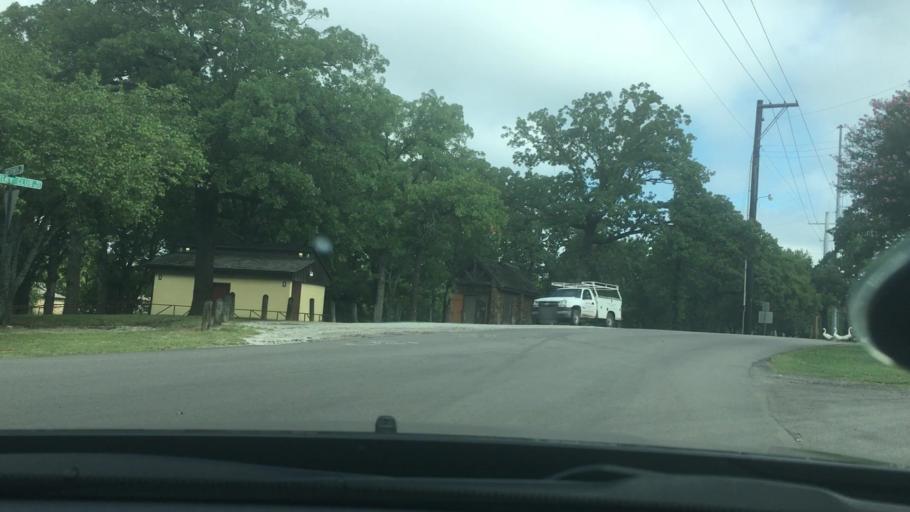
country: US
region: Oklahoma
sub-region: Pontotoc County
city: Ada
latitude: 34.7660
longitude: -96.6524
